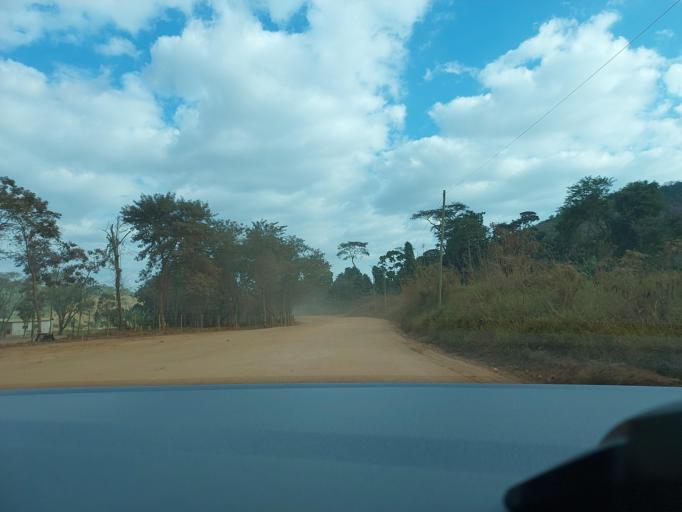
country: BR
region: Minas Gerais
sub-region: Visconde Do Rio Branco
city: Visconde do Rio Branco
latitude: -20.8544
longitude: -42.6671
